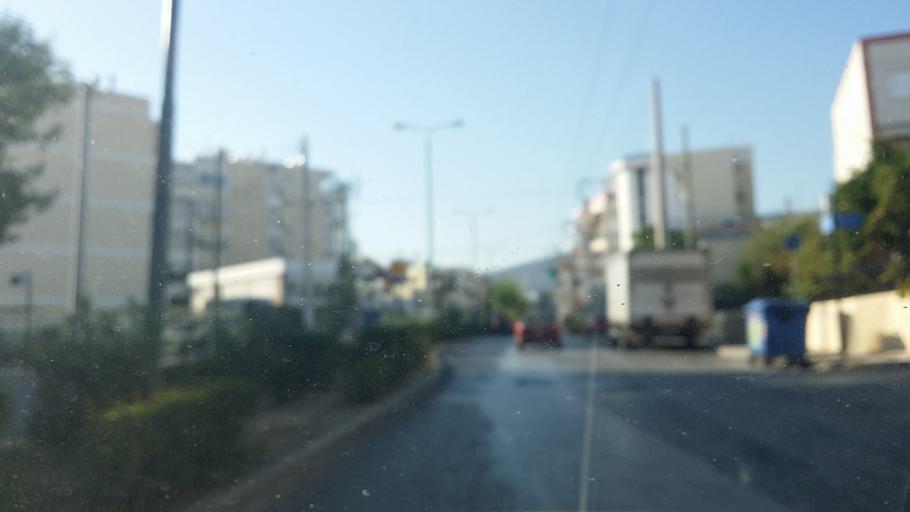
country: GR
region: Attica
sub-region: Nomarchia Athinas
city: Ilion
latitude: 38.0287
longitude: 23.6962
